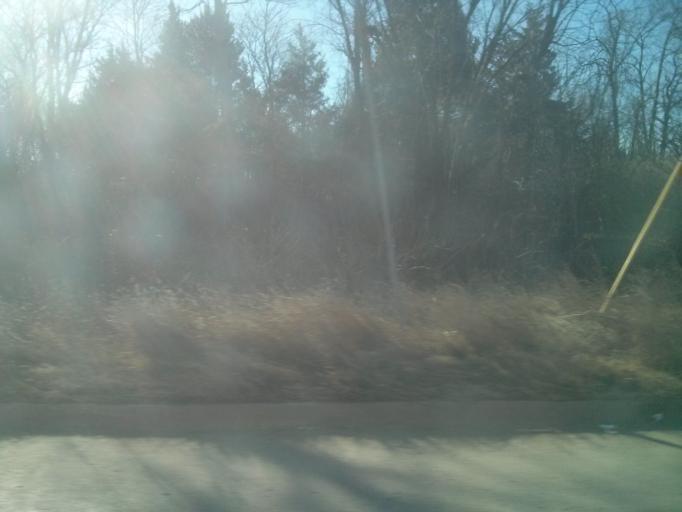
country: US
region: Oklahoma
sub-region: Tulsa County
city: Owasso
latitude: 36.1770
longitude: -95.8863
